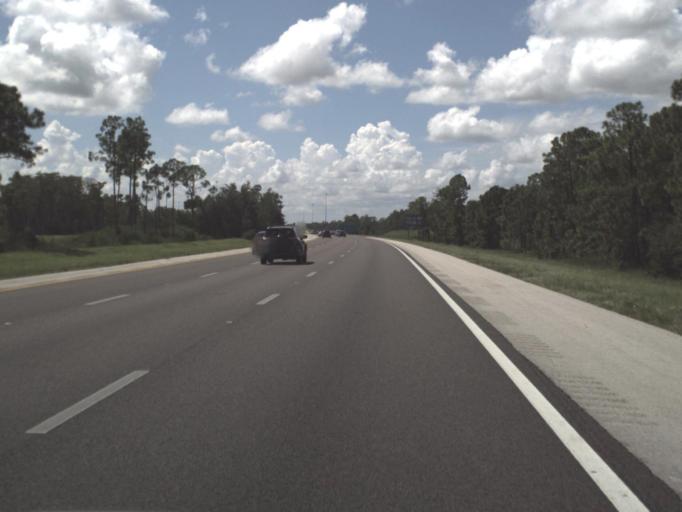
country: US
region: Florida
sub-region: Lee County
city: Gateway
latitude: 26.5579
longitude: -81.7951
